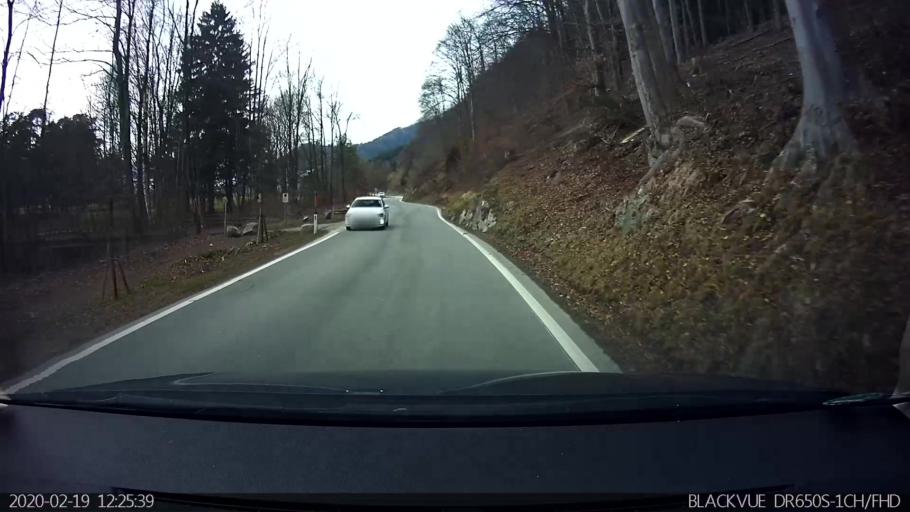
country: AT
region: Tyrol
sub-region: Politischer Bezirk Schwaz
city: Stans
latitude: 47.3795
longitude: 11.7327
